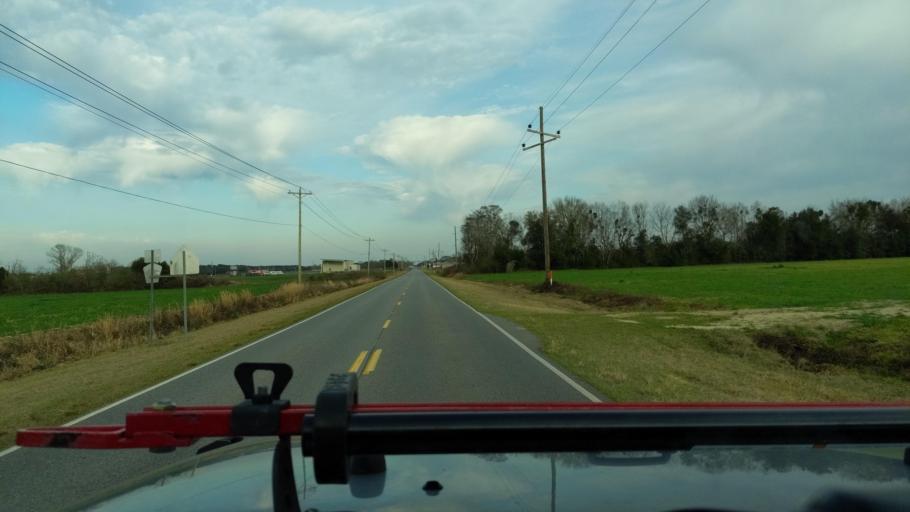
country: US
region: Alabama
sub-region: Baldwin County
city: Foley
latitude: 30.4581
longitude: -87.6978
